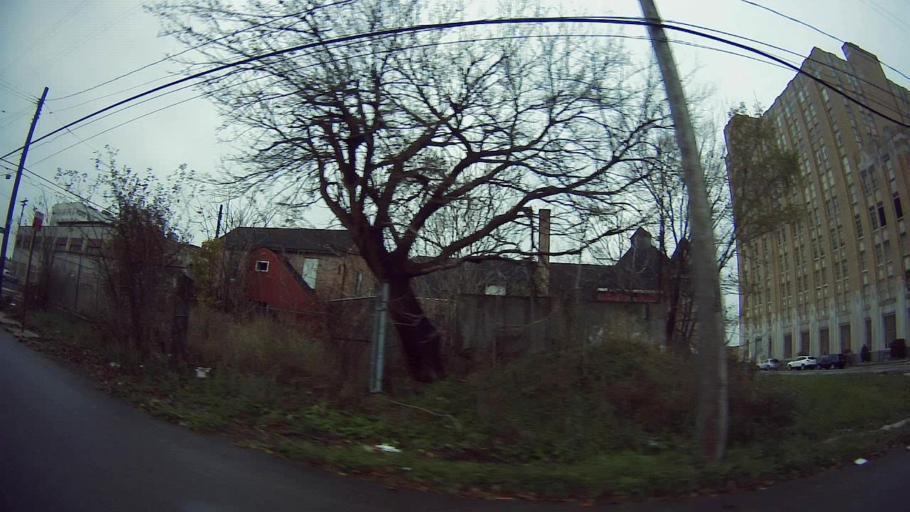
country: US
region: Michigan
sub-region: Wayne County
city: Hamtramck
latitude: 42.3729
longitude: -83.0723
